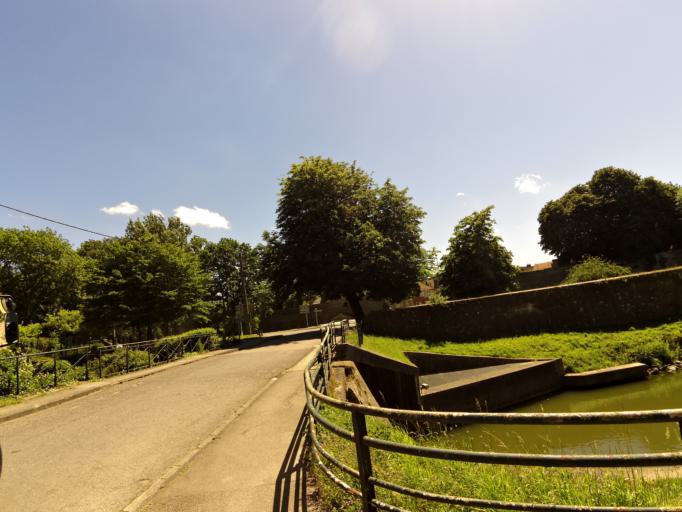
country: FR
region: Nord-Pas-de-Calais
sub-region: Departement du Nord
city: Bergues
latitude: 50.9719
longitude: 2.4331
